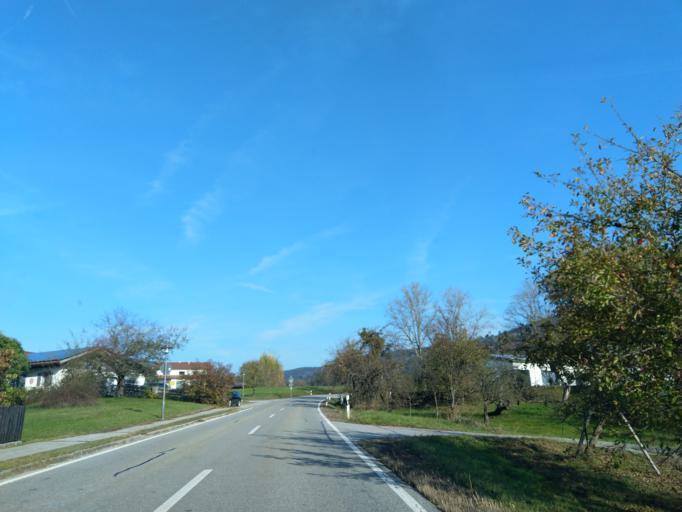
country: DE
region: Bavaria
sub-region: Lower Bavaria
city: Lalling
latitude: 48.8499
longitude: 13.1389
